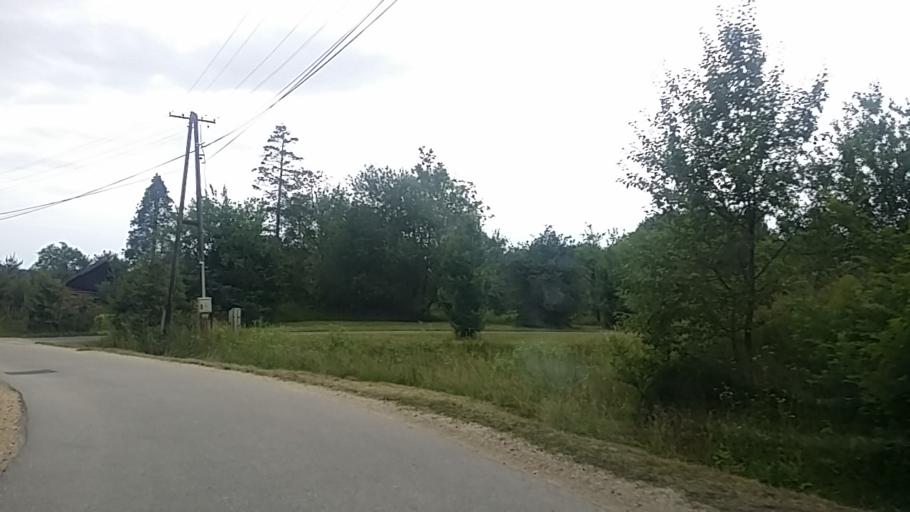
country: SI
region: Hodos-Hodos
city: Hodos
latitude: 46.8458
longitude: 16.4223
